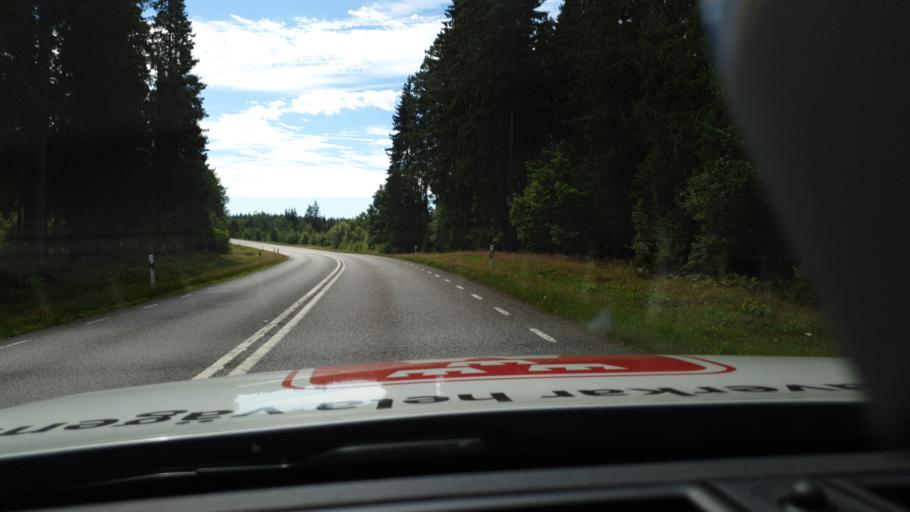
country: SE
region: Kronoberg
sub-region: Vaxjo Kommun
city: Lammhult
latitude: 57.2273
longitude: 14.5076
